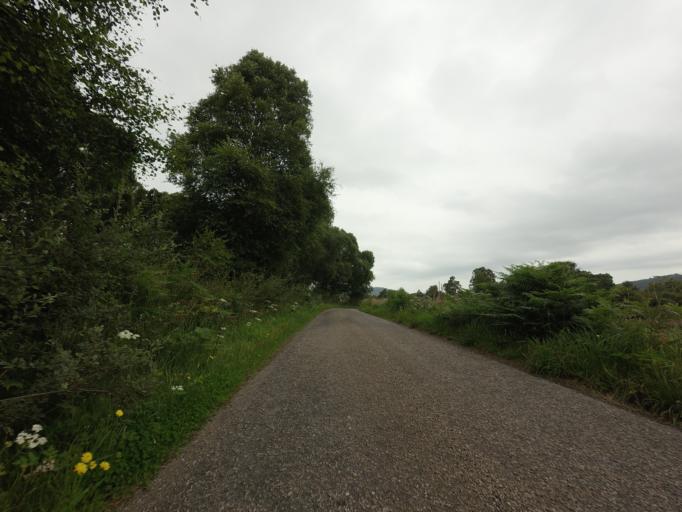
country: GB
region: Scotland
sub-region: Highland
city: Evanton
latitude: 57.9059
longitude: -4.3920
